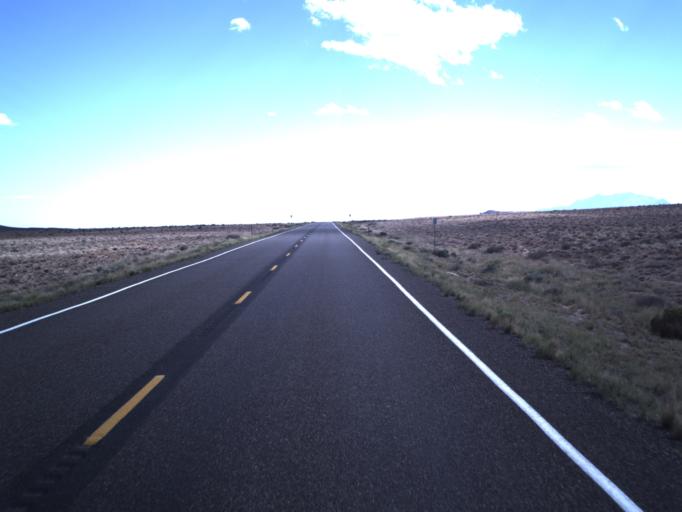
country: US
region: Utah
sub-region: Emery County
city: Ferron
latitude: 38.2804
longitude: -110.6624
